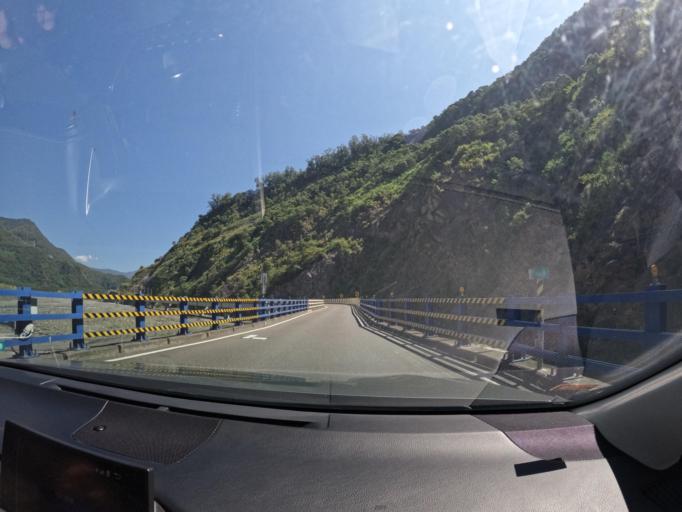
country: TW
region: Taiwan
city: Yujing
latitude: 23.1898
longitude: 120.7906
